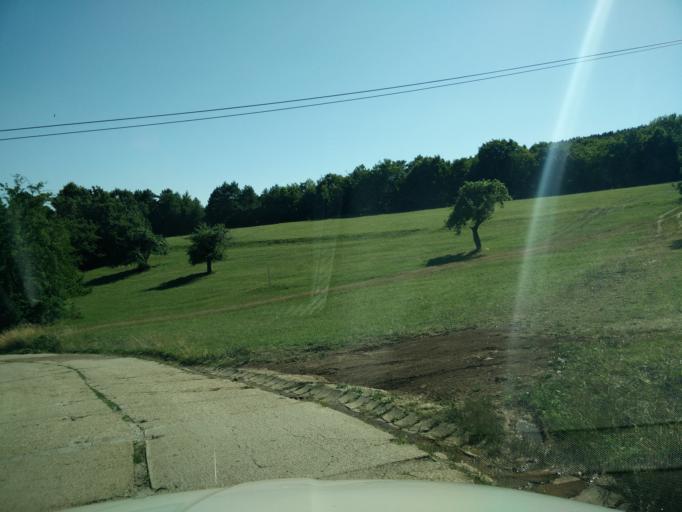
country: SK
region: Nitriansky
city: Bojnice
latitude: 48.7890
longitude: 18.5752
